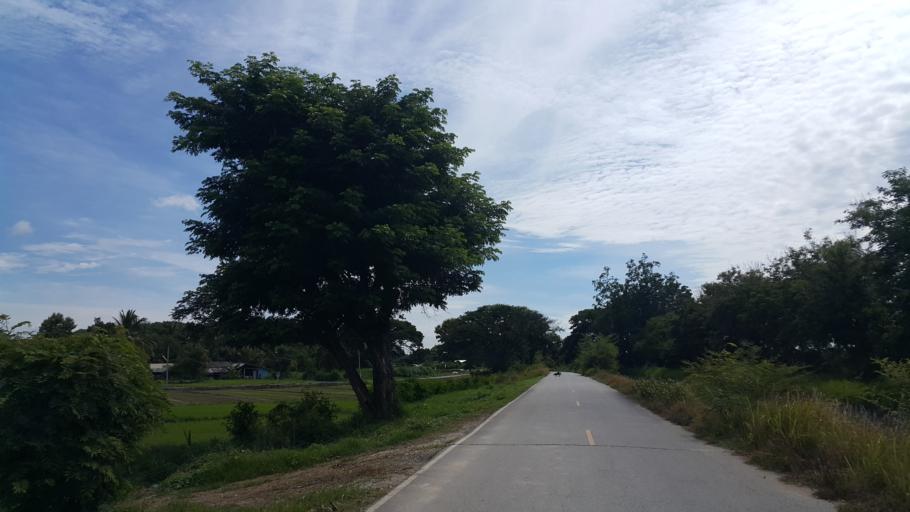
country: TH
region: Chiang Mai
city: Mae On
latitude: 18.7274
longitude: 99.1923
